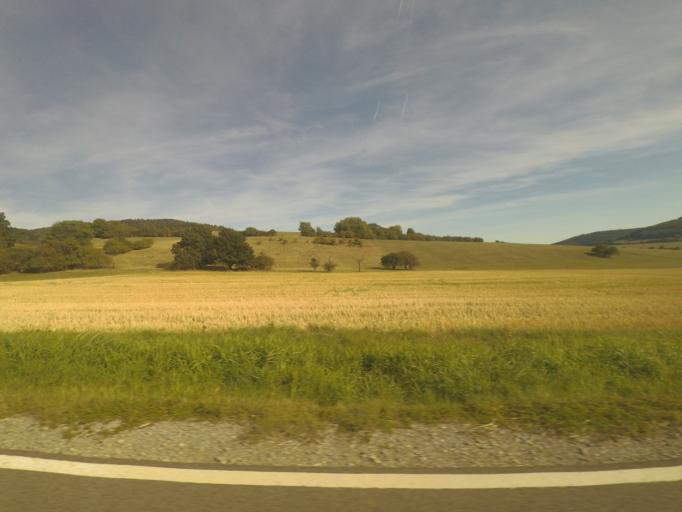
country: DE
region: Thuringia
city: Oberkatz
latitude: 50.5716
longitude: 10.2389
